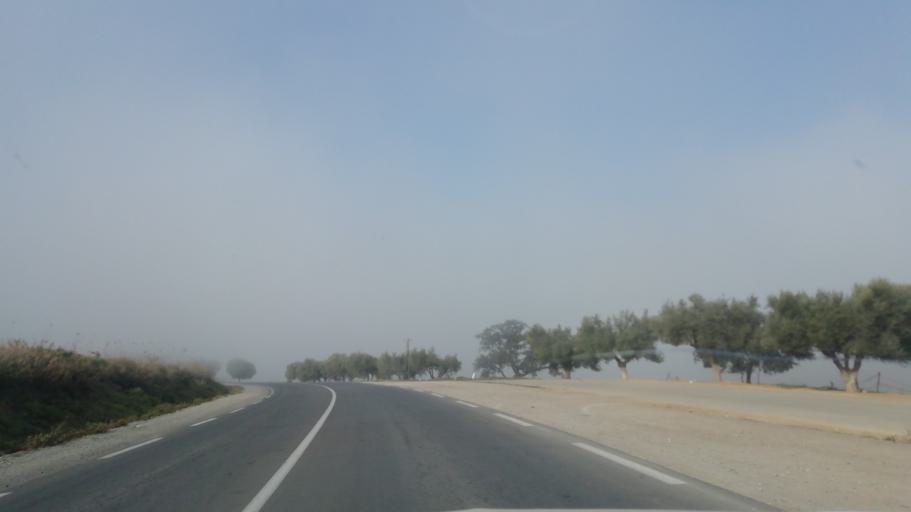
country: DZ
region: Mascara
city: Mascara
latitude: 35.5270
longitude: 0.3453
